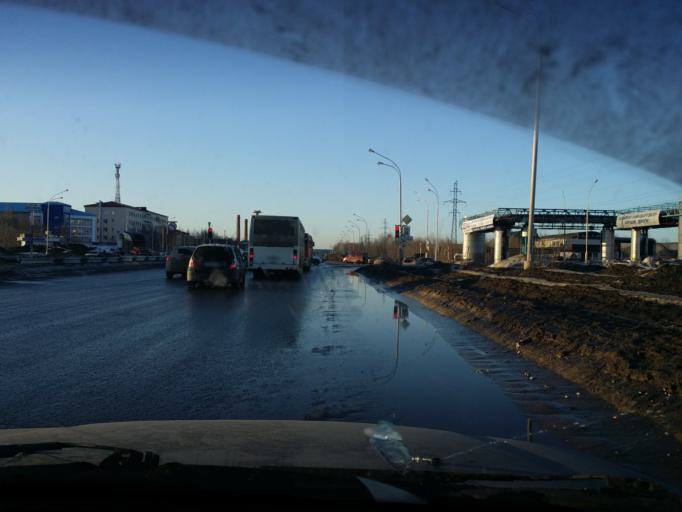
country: RU
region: Khanty-Mansiyskiy Avtonomnyy Okrug
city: Nizhnevartovsk
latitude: 60.9381
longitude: 76.5306
